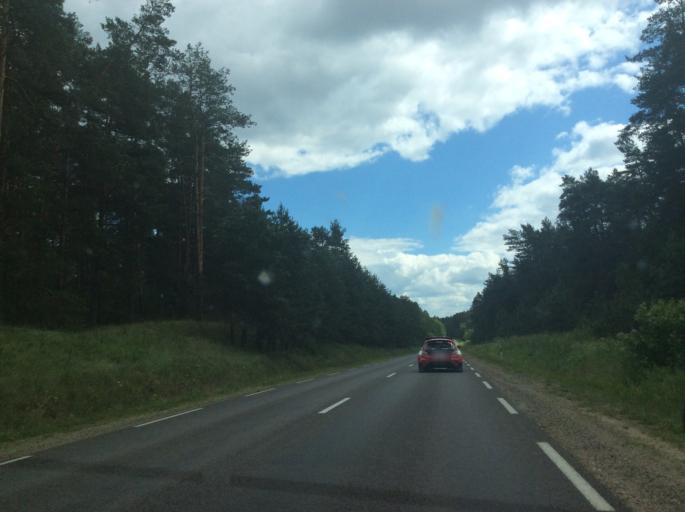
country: LT
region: Alytaus apskritis
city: Druskininkai
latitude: 54.0436
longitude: 23.9444
